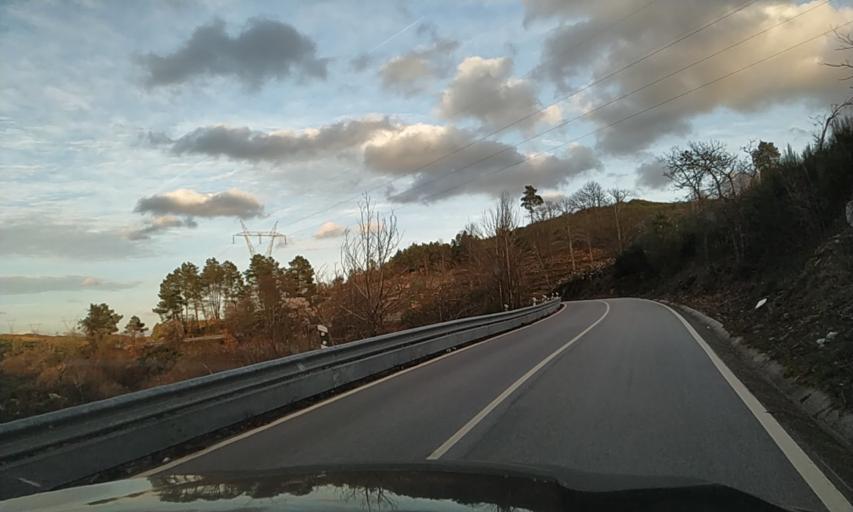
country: PT
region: Braganca
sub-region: Carrazeda de Ansiaes
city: Carrazeda de Anciaes
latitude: 41.2093
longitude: -7.3333
